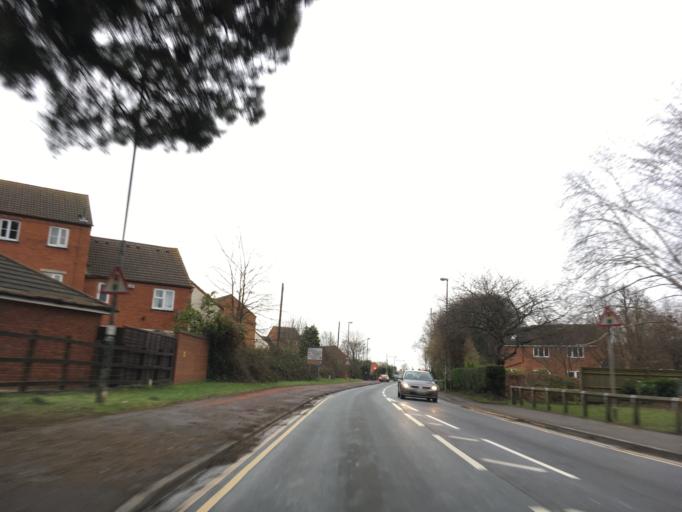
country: GB
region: England
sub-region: Gloucestershire
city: Churchdown
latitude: 51.8871
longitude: -2.1883
